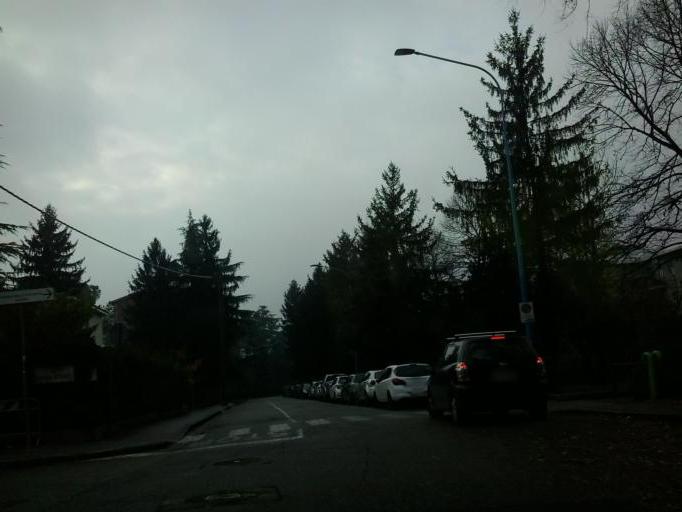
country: IT
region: Lombardy
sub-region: Provincia di Brescia
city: Bovezzo
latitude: 45.5689
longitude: 10.2332
